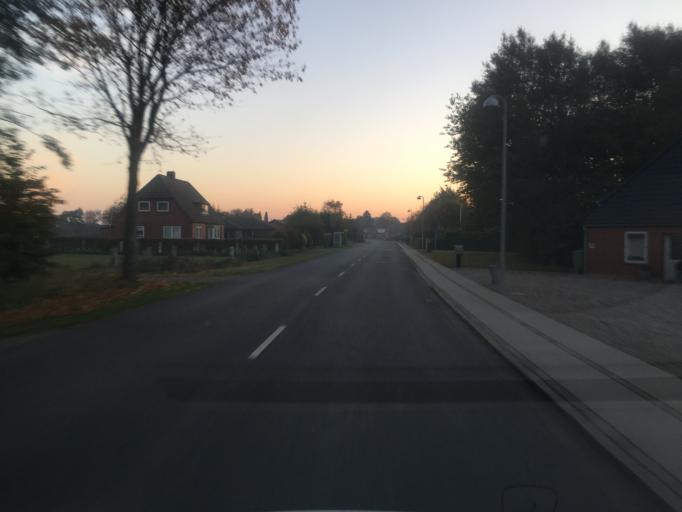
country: DE
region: Schleswig-Holstein
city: Bramstedtlund
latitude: 54.9484
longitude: 9.0957
